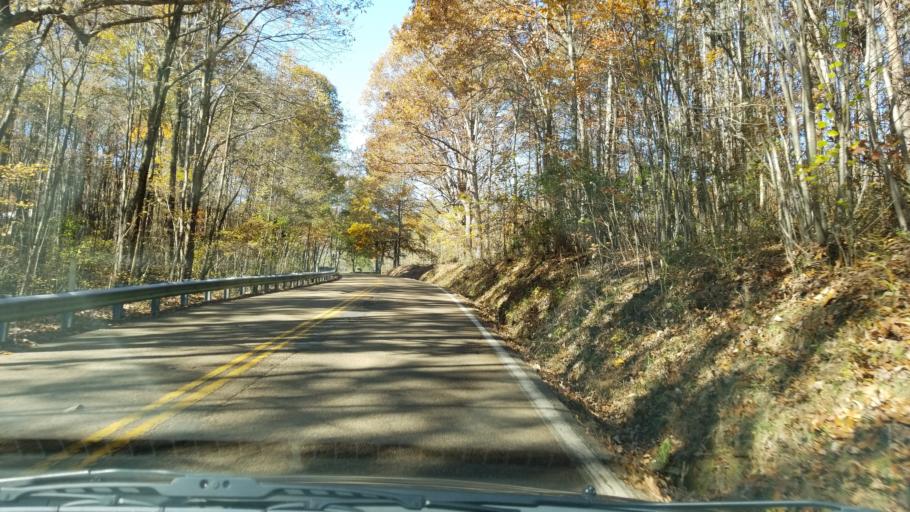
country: US
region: Tennessee
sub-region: Hamilton County
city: Falling Water
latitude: 35.2189
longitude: -85.2686
